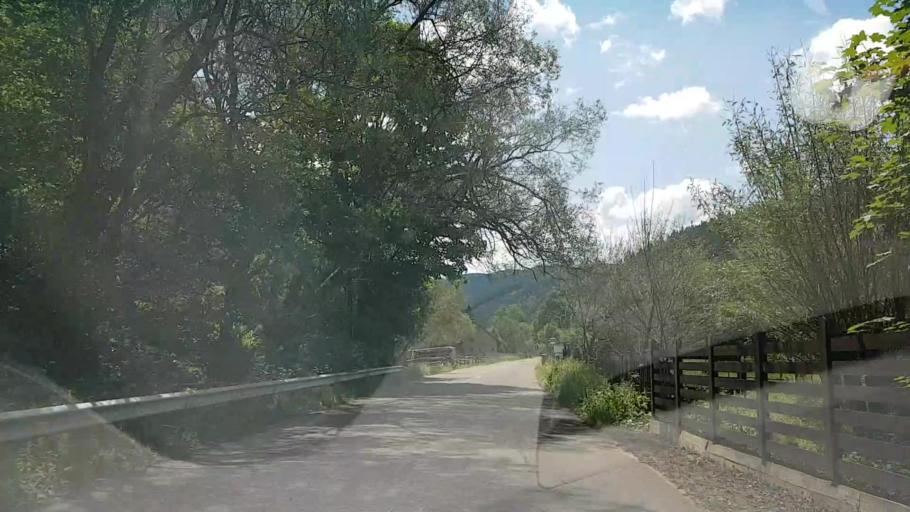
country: RO
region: Suceava
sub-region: Comuna Pojorata
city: Pojorata
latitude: 47.4925
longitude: 25.4849
